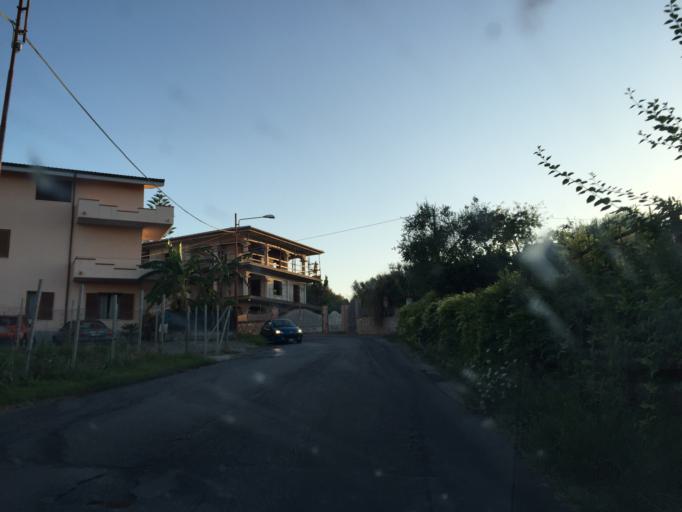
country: IT
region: Calabria
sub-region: Provincia di Vibo-Valentia
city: Pannaconi
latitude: 38.6948
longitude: 16.0450
